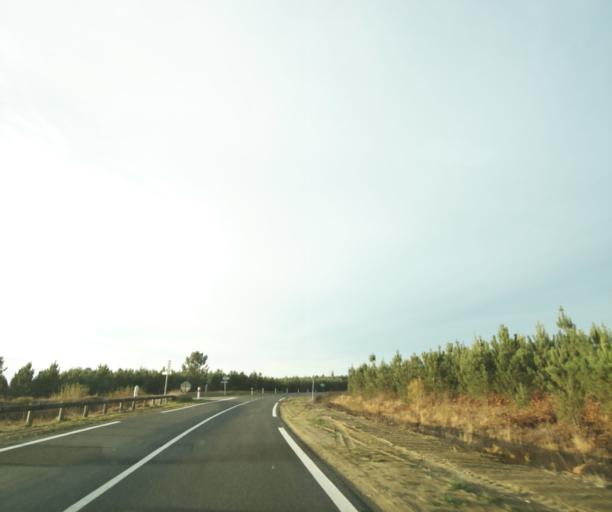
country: FR
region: Aquitaine
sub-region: Departement des Landes
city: Gabarret
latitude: 44.0857
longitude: -0.0923
